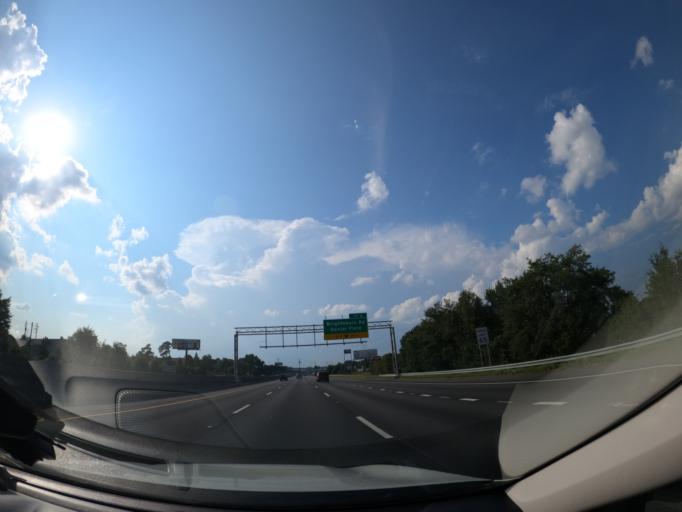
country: US
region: Georgia
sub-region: Columbia County
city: Martinez
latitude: 33.4584
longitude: -82.0776
